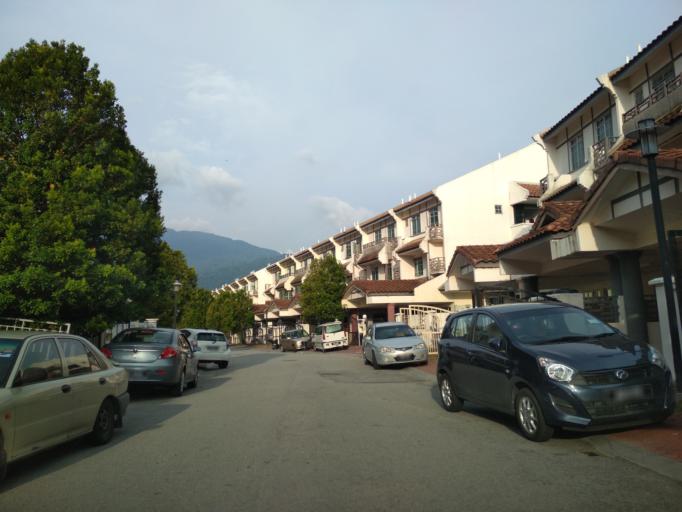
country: MY
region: Perak
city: Kampar
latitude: 4.3297
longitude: 101.1350
